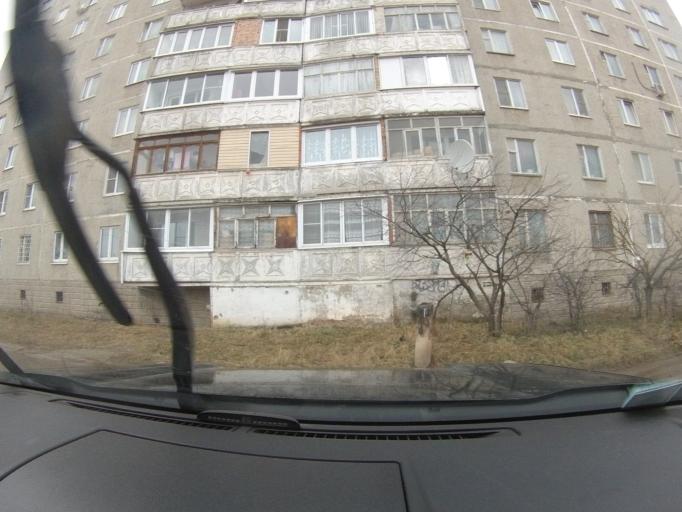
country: RU
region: Moskovskaya
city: Peski
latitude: 55.2709
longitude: 38.7544
